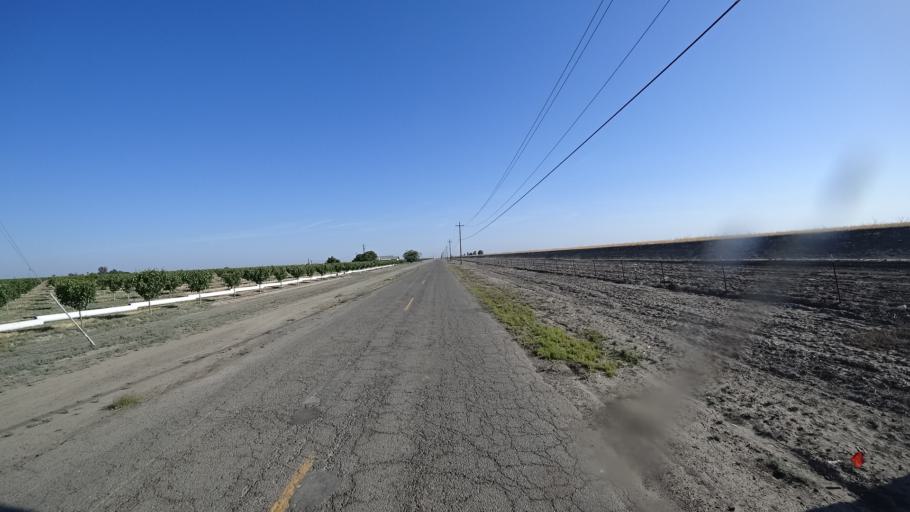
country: US
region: California
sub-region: Kings County
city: Corcoran
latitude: 36.1247
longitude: -119.5543
